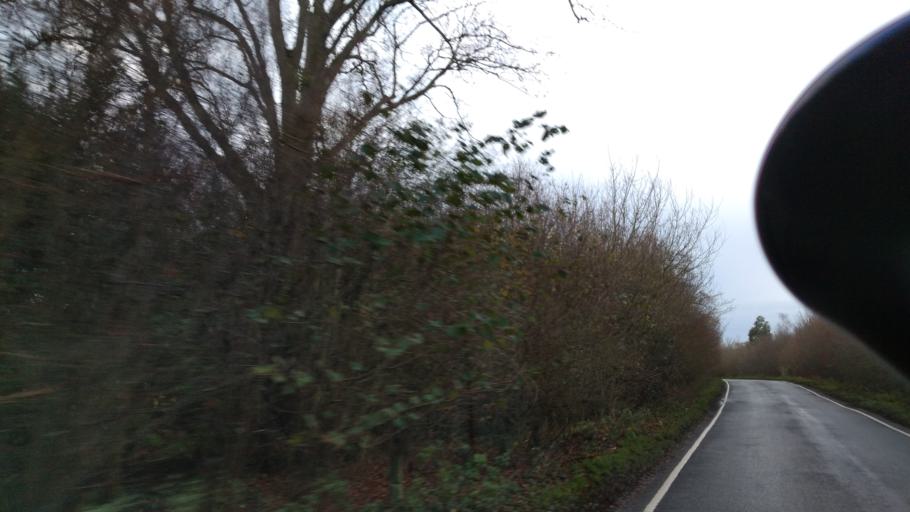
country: GB
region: England
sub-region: Borough of Swindon
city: Highworth
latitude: 51.6160
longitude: -1.6937
